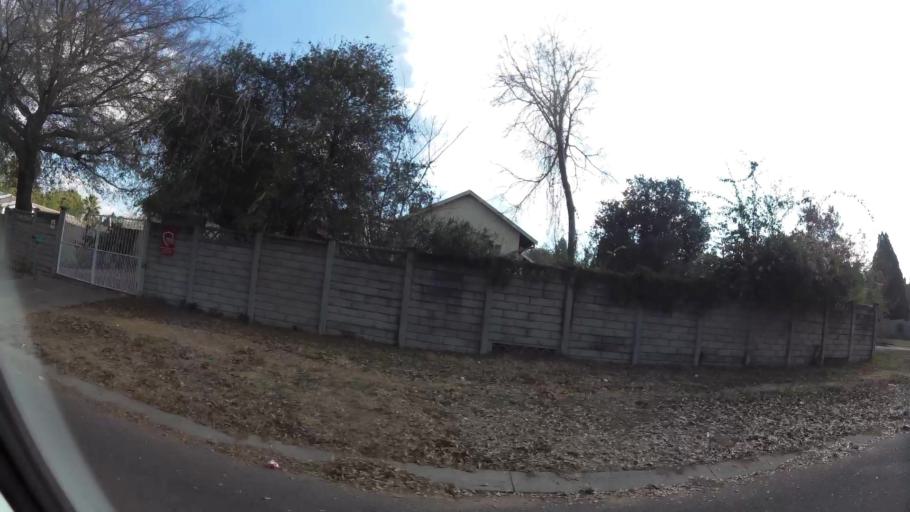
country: ZA
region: Gauteng
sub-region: City of Johannesburg Metropolitan Municipality
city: Midrand
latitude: -25.9973
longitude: 28.1069
